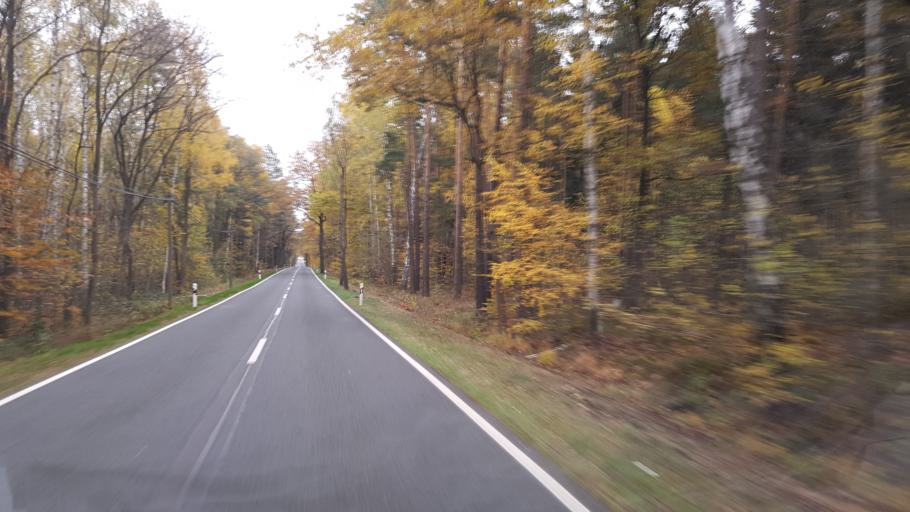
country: DE
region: Brandenburg
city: Crinitz
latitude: 51.7468
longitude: 13.7872
